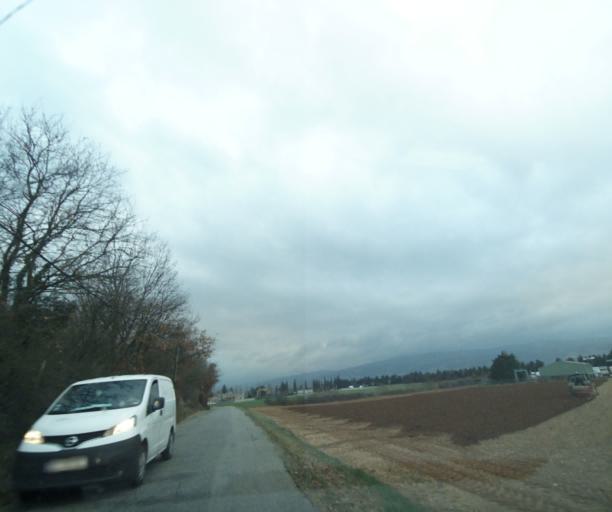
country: FR
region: Rhone-Alpes
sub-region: Departement de la Drome
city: Bourg-les-Valence
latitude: 44.9766
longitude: 4.9018
